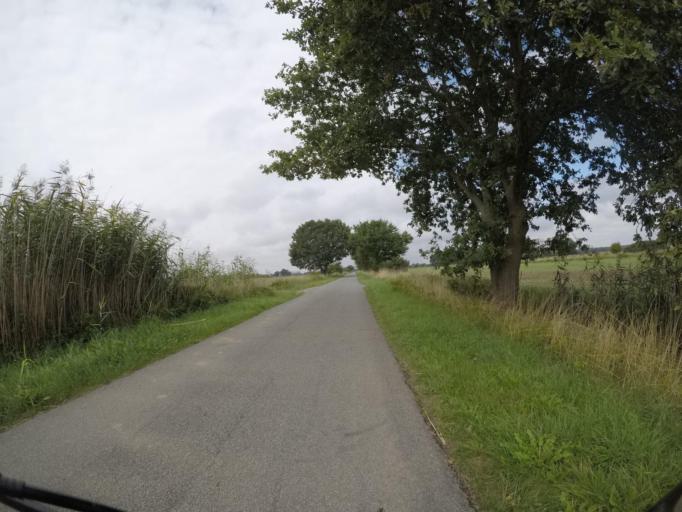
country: DE
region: Lower Saxony
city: Neu Darchau
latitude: 53.2895
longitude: 10.9039
